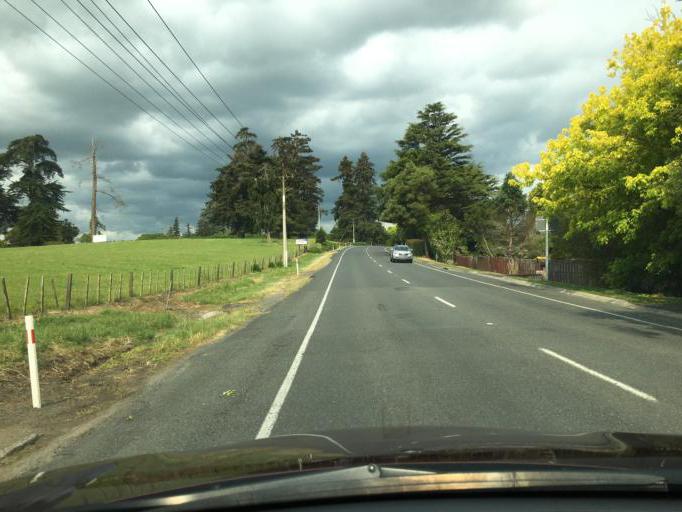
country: NZ
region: Waikato
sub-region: Waipa District
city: Cambridge
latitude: -38.0068
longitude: 175.3504
